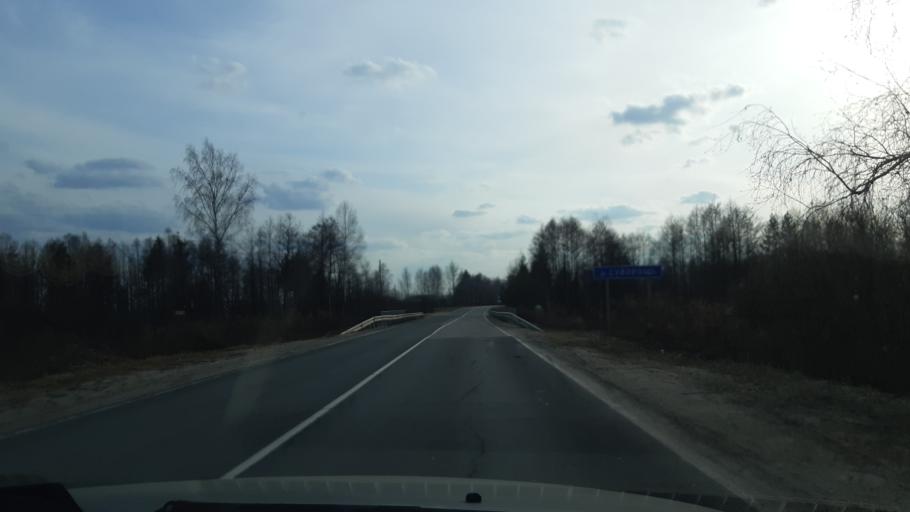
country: RU
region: Vladimir
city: Luknovo
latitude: 56.1793
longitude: 42.0097
